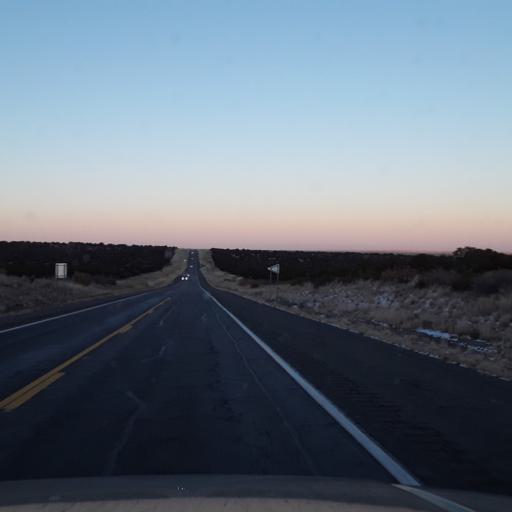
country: US
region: New Mexico
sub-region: Torrance County
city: Estancia
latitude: 34.5237
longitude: -105.3288
